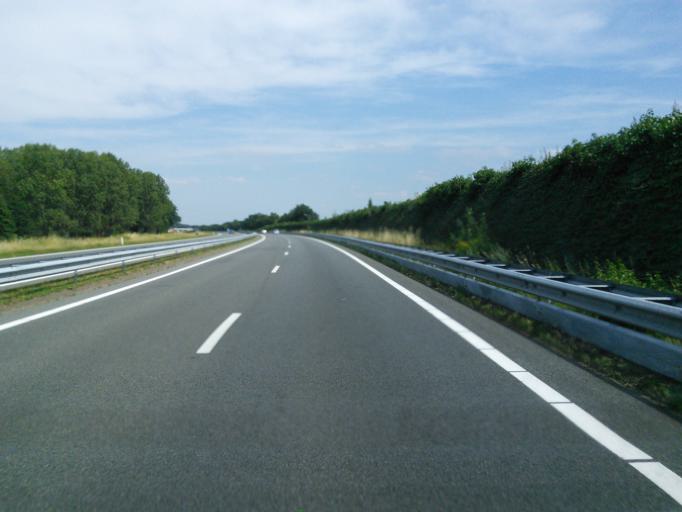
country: NL
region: Limburg
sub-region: Gemeente Roermond
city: Leeuwen
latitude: 51.1994
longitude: 6.0448
